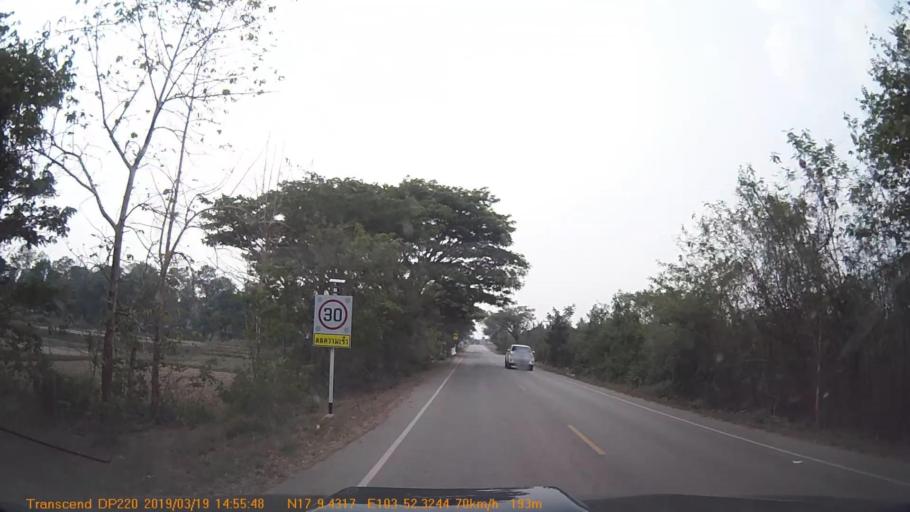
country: TH
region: Sakon Nakhon
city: Kut Bak
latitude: 17.1573
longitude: 103.8719
